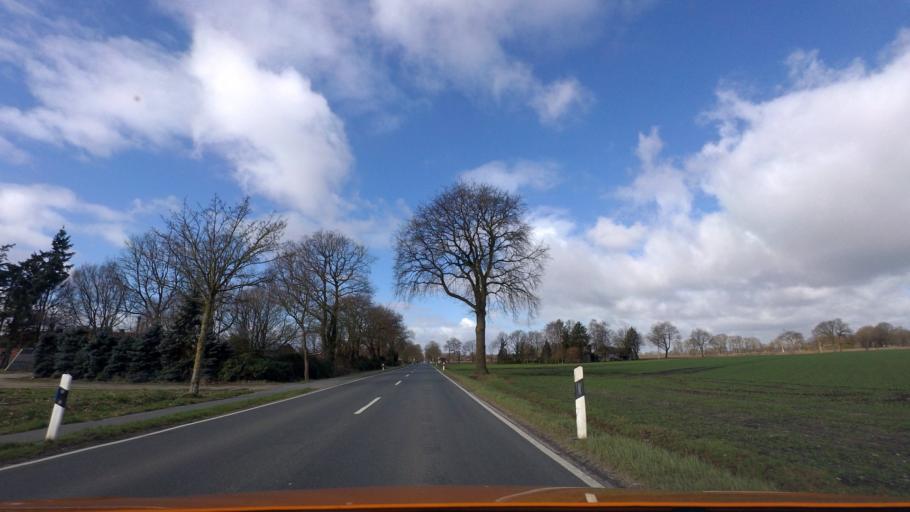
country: DE
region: Lower Saxony
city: Friesoythe
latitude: 53.0159
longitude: 7.9028
